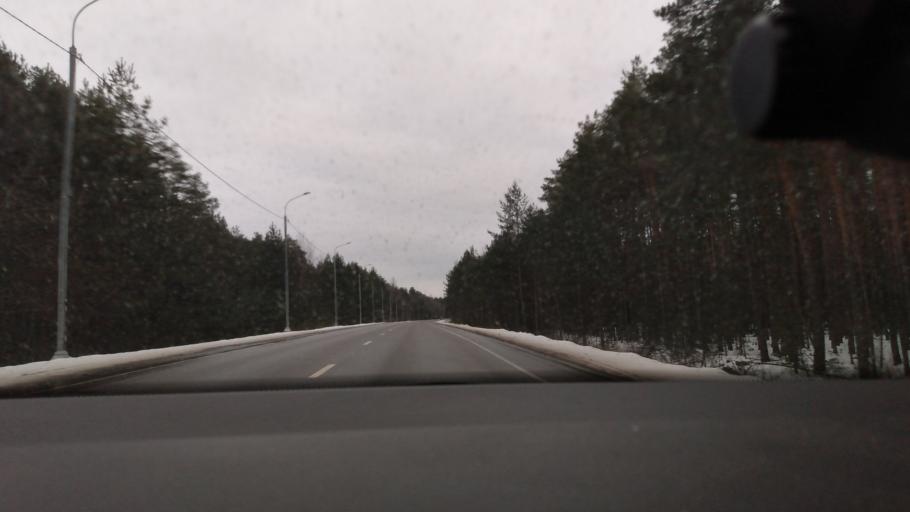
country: RU
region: Moskovskaya
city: Il'inskiy Pogost
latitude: 55.4762
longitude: 38.9484
